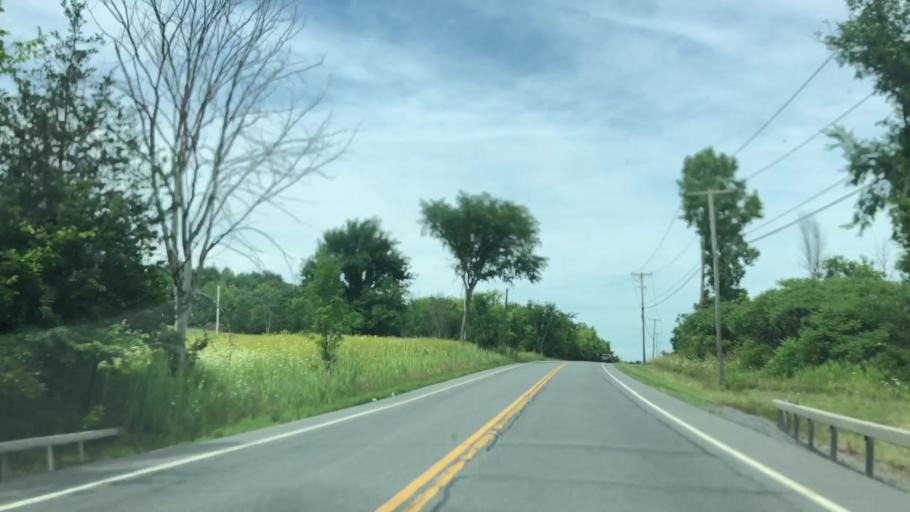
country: US
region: New York
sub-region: Washington County
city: Whitehall
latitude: 43.5203
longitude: -73.4141
